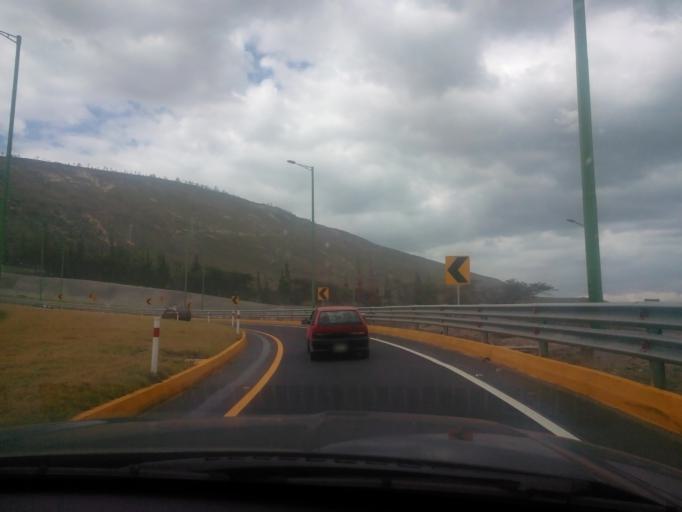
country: EC
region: Pichincha
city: Quito
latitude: -0.0880
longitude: -78.3922
